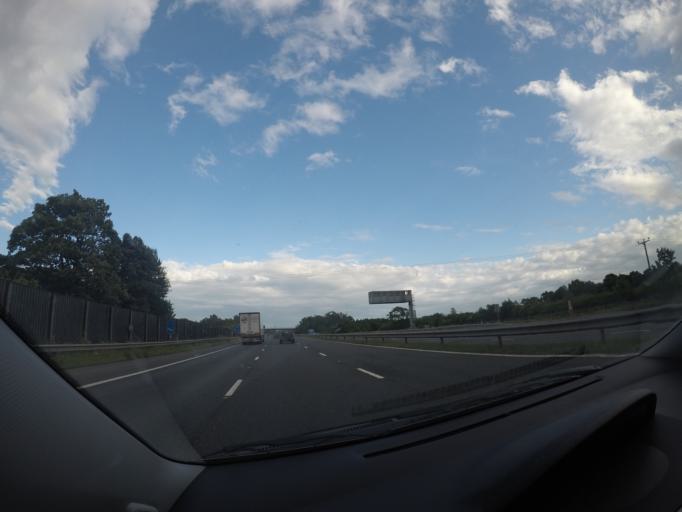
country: GB
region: England
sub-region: Cumbria
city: Carlisle
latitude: 54.9567
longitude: -2.9865
